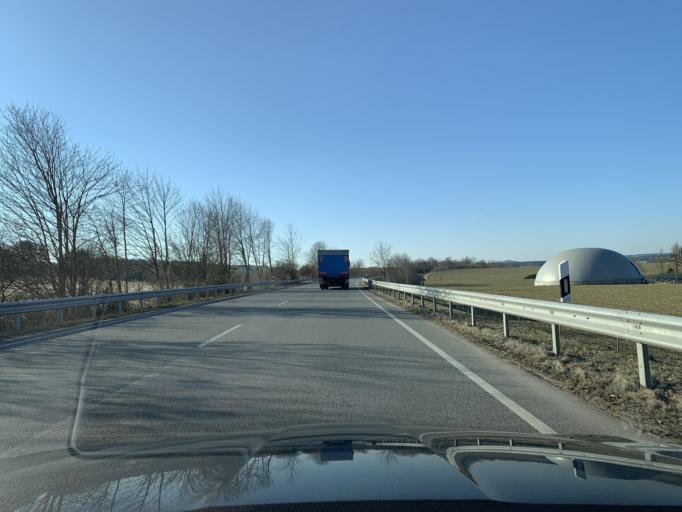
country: DE
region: Bavaria
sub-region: Upper Palatinate
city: Schonthal
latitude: 49.3324
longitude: 12.6174
